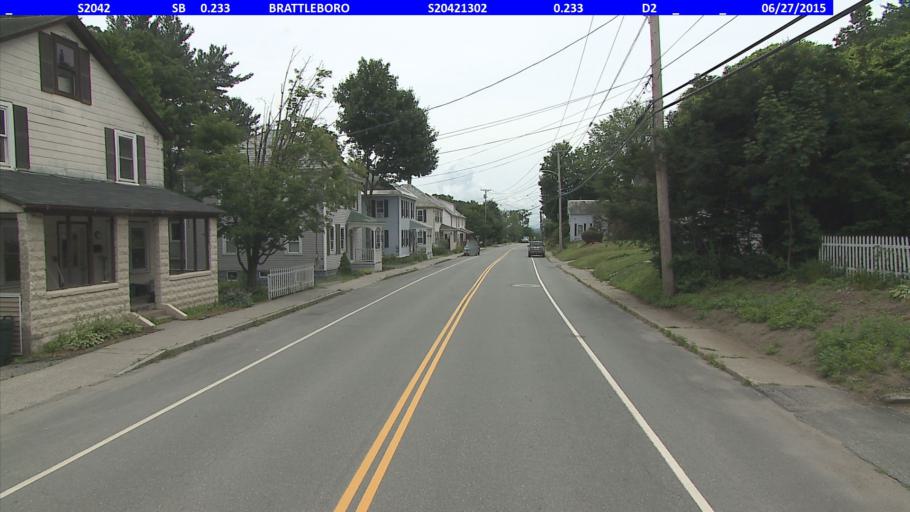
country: US
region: Vermont
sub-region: Windham County
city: Brattleboro
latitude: 42.8407
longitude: -72.5556
